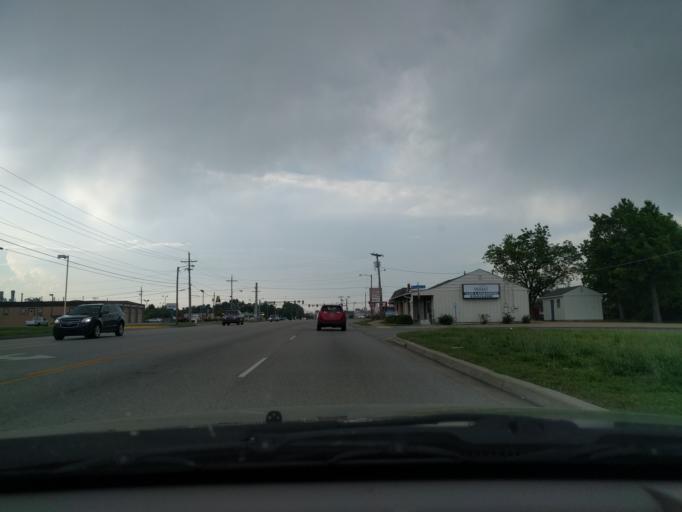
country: US
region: Oklahoma
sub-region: Tulsa County
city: Broken Arrow
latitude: 36.0590
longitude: -95.7974
